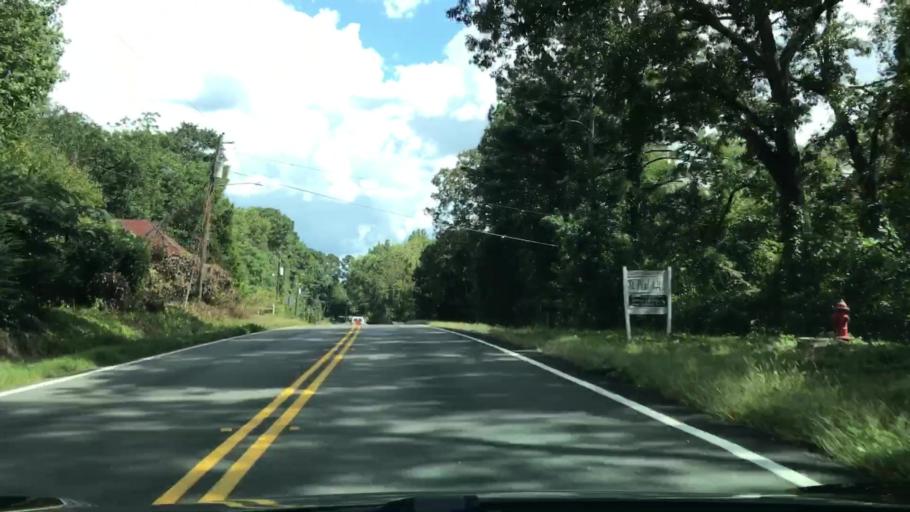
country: US
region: Georgia
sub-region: Greene County
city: Union Point
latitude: 33.5385
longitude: -83.0864
